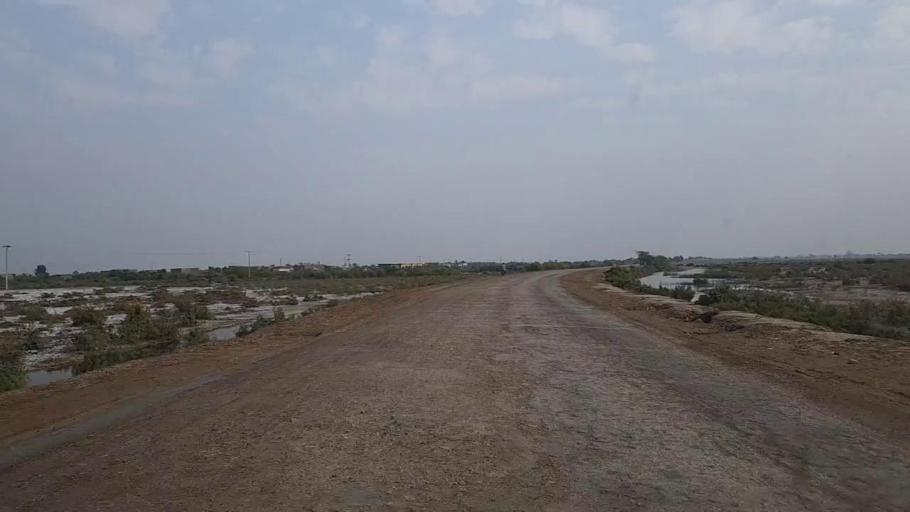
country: PK
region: Sindh
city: Mirwah Gorchani
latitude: 25.3797
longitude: 69.0938
